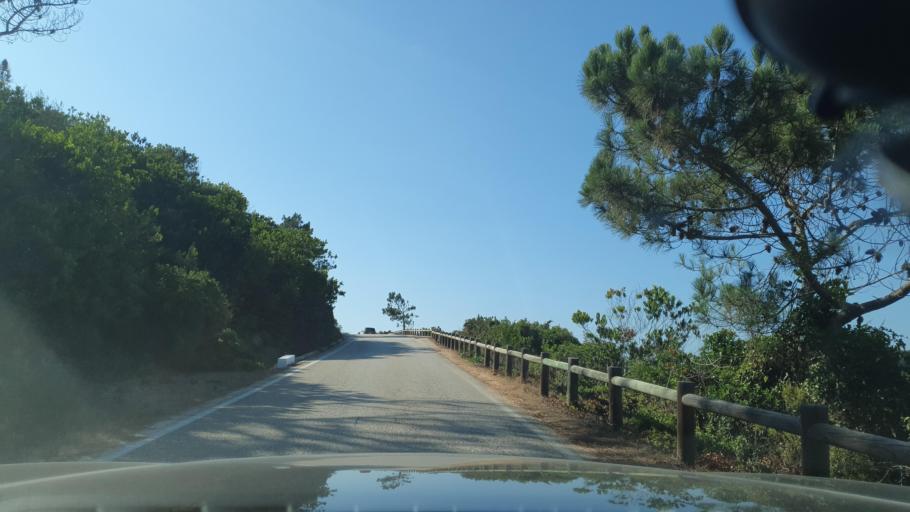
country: PT
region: Beja
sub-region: Odemira
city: Sao Teotonio
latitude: 37.4377
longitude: -8.7953
